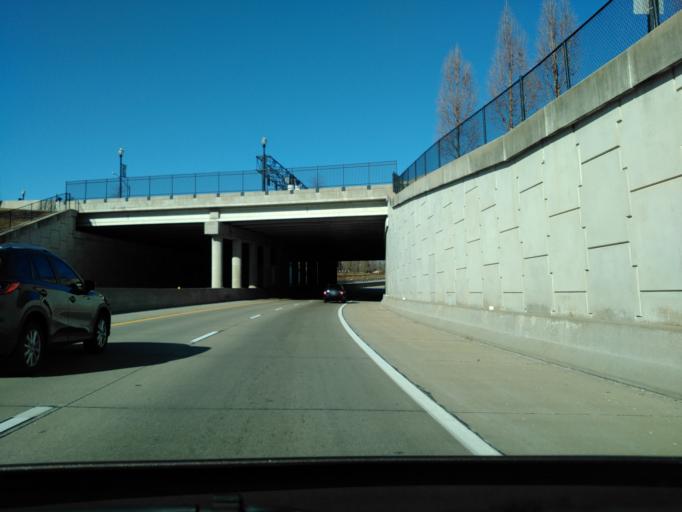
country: US
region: Missouri
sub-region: Saint Louis County
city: Valley Park
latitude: 38.5671
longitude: -90.4999
